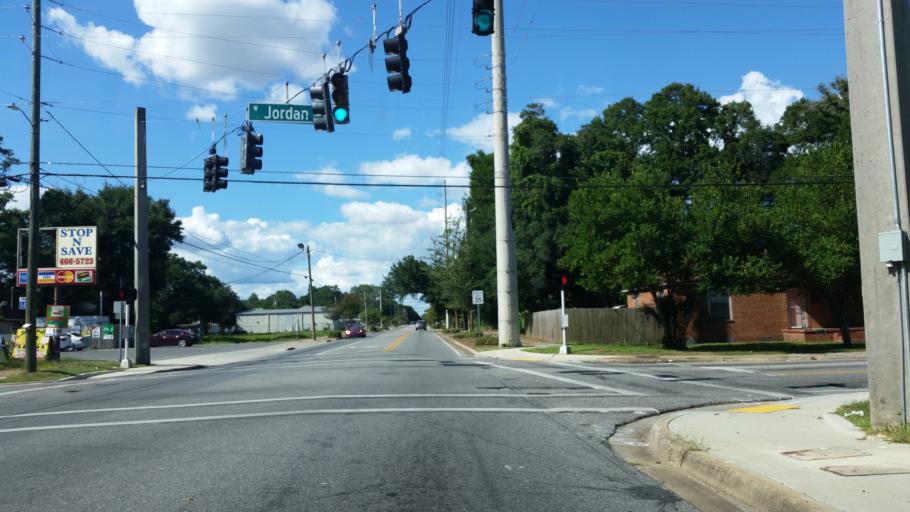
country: US
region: Florida
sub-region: Escambia County
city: Goulding
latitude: 30.4334
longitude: -87.2293
